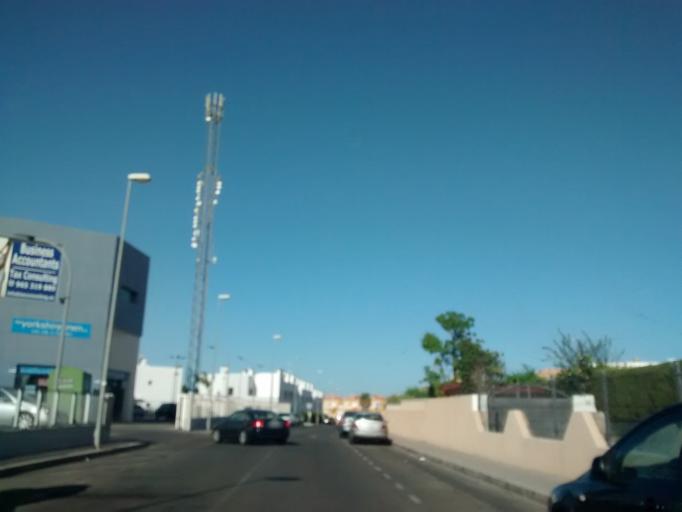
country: ES
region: Valencia
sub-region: Provincia de Alicante
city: Torrevieja
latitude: 37.9262
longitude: -0.7342
